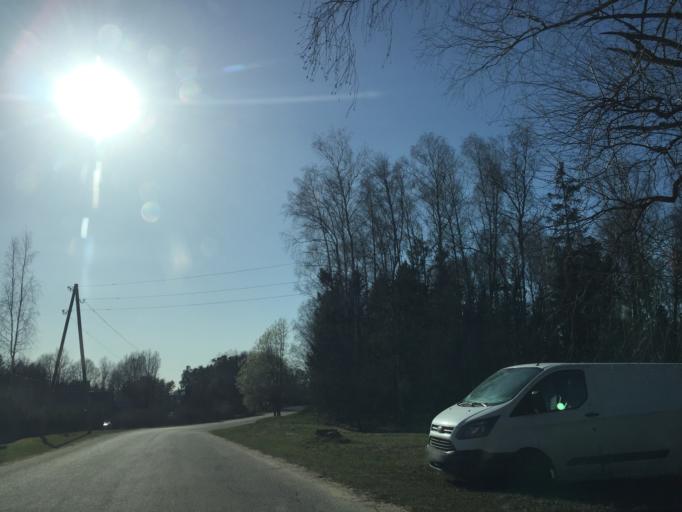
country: LV
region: Malpils
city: Malpils
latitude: 57.0815
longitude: 25.0784
